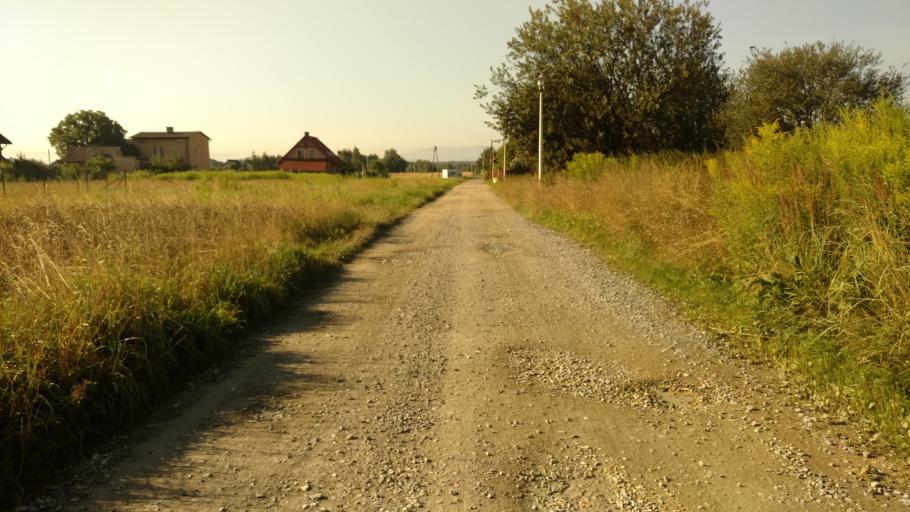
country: PL
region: Silesian Voivodeship
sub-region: Powiat pszczynski
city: Pszczyna
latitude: 49.9907
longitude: 18.9674
